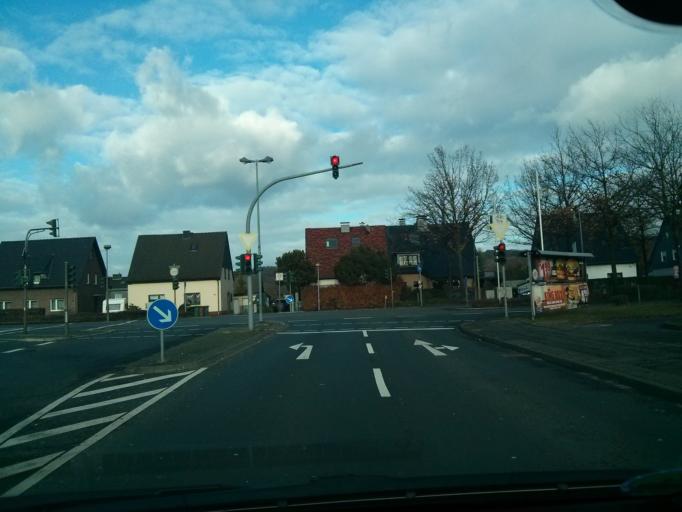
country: DE
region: North Rhine-Westphalia
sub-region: Regierungsbezirk Koln
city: Hennef
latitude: 50.7796
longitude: 7.2718
